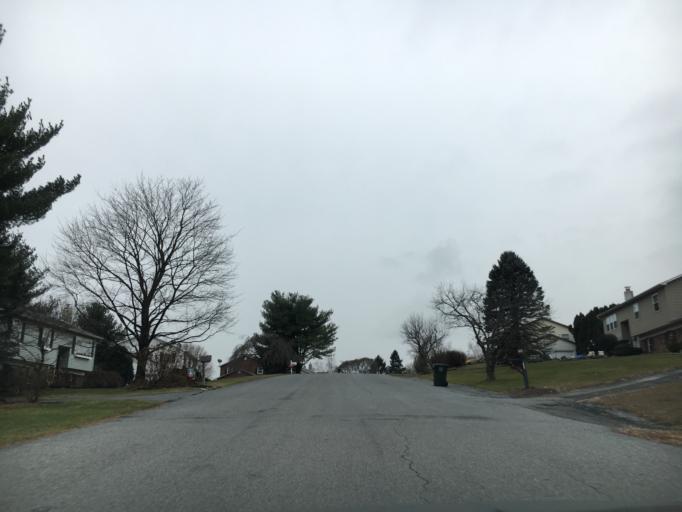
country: US
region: Pennsylvania
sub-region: Lehigh County
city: Schnecksville
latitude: 40.7039
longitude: -75.5764
